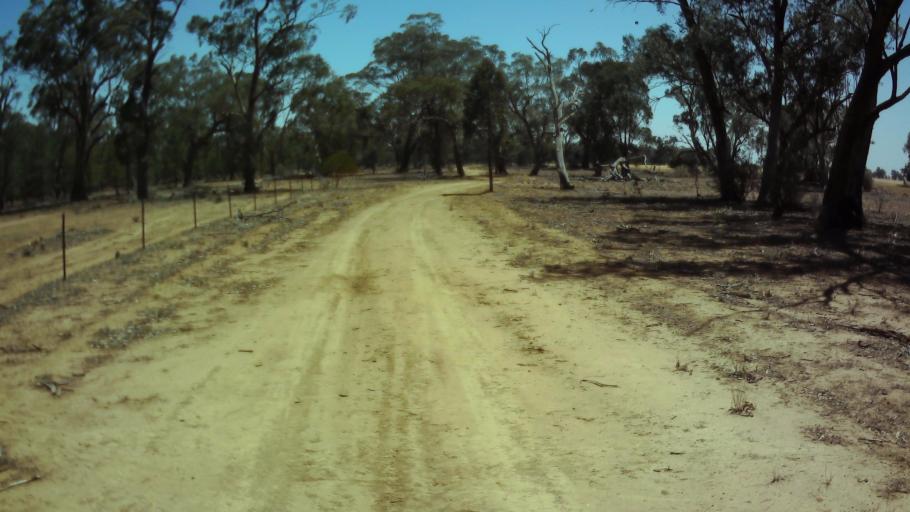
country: AU
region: New South Wales
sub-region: Weddin
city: Grenfell
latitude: -34.0678
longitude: 147.7970
